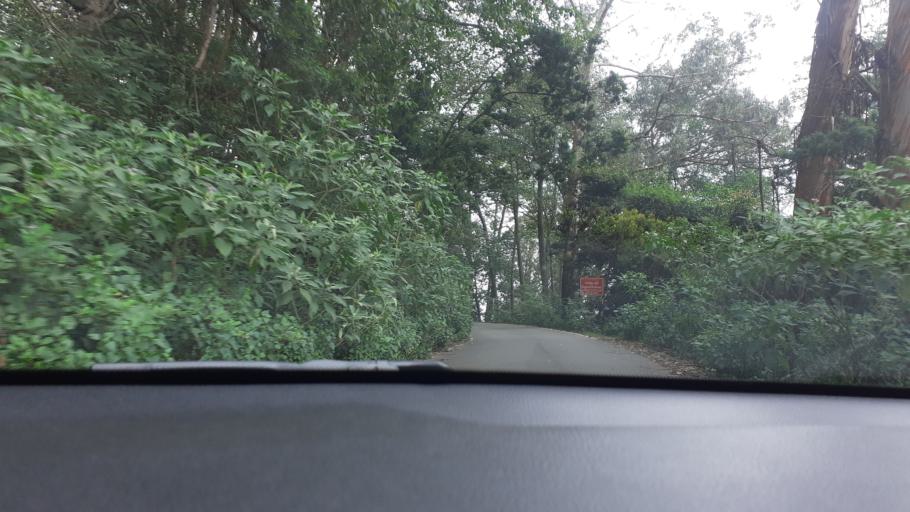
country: IN
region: Tamil Nadu
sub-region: Dindigul
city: Kodaikanal
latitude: 10.2404
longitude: 77.4220
